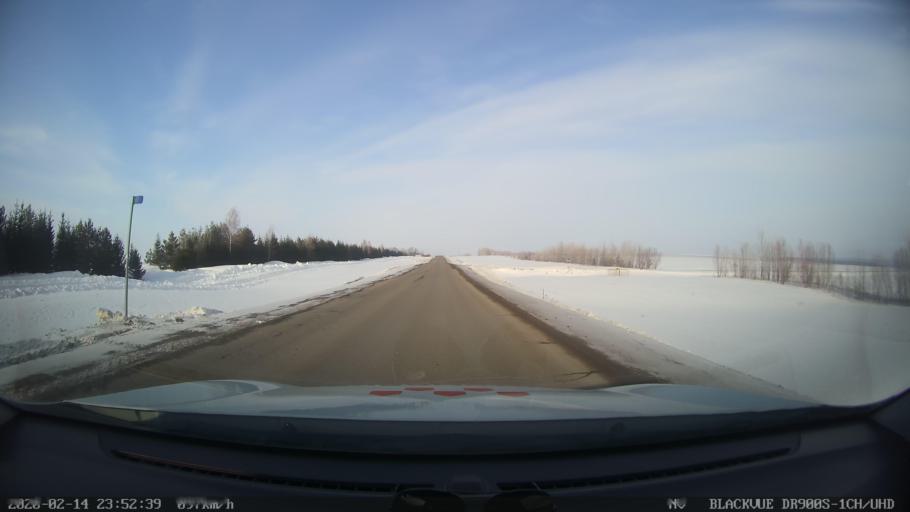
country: RU
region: Tatarstan
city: Kuybyshevskiy Zaton
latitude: 55.2816
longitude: 49.1439
